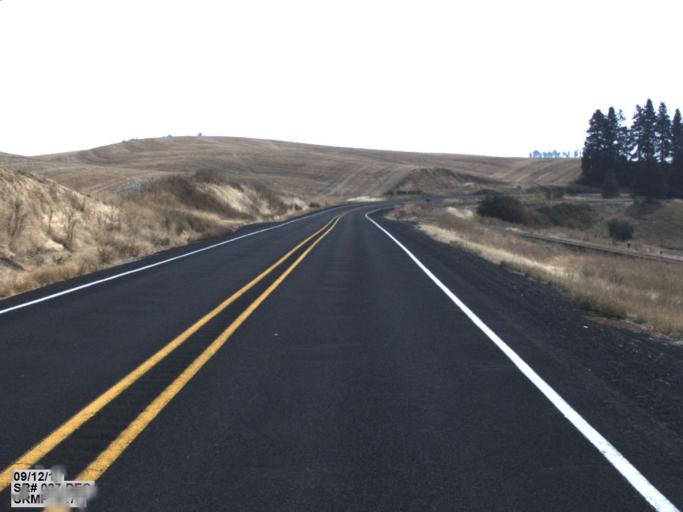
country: US
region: Washington
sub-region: Whitman County
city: Pullman
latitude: 46.9675
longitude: -117.1131
